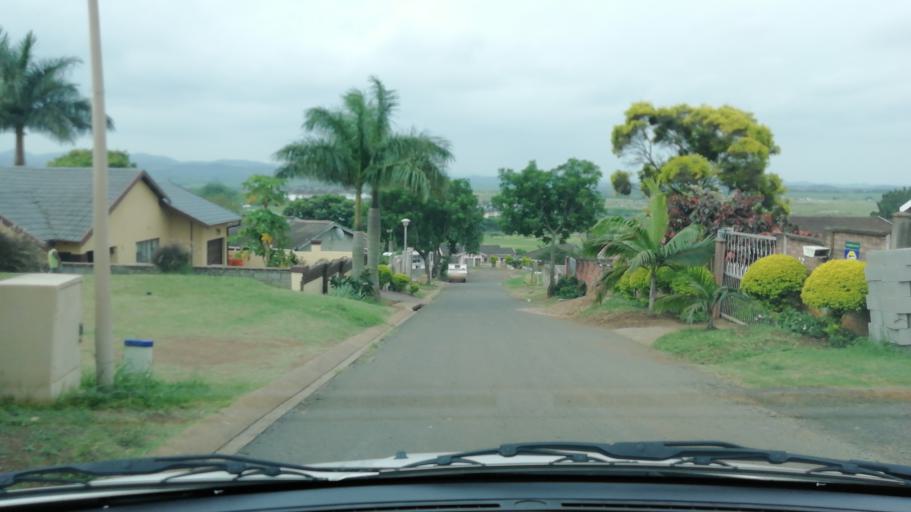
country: ZA
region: KwaZulu-Natal
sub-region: uThungulu District Municipality
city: Empangeni
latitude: -28.7381
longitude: 31.8787
